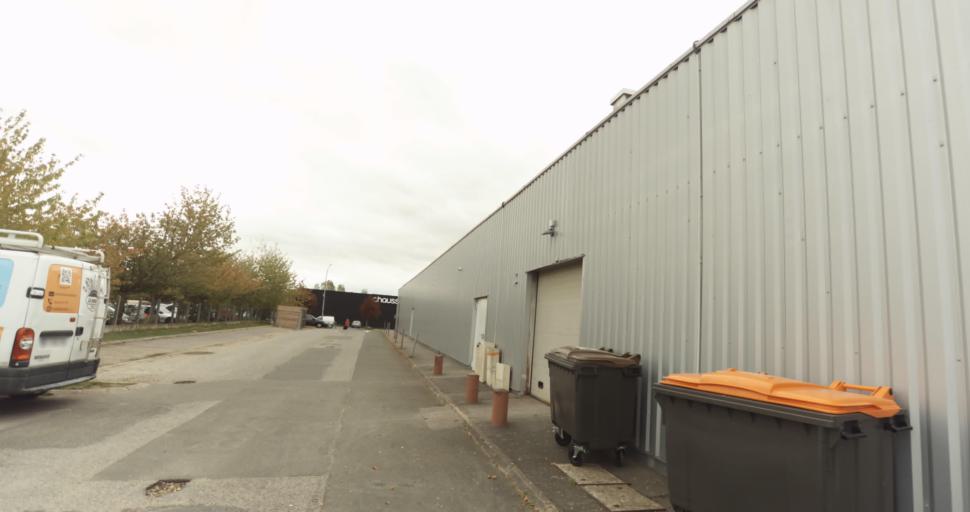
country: FR
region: Centre
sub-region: Departement d'Eure-et-Loir
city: Vernouillet
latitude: 48.7184
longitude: 1.3707
